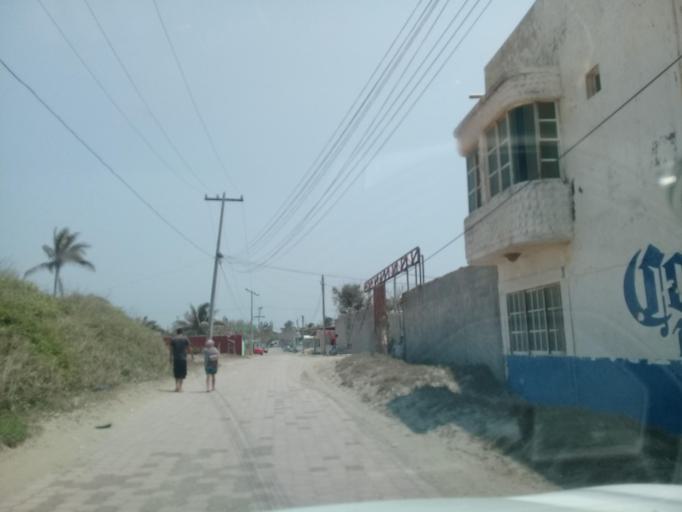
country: MX
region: Veracruz
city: Anton Lizardo
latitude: 19.0614
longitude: -95.9949
